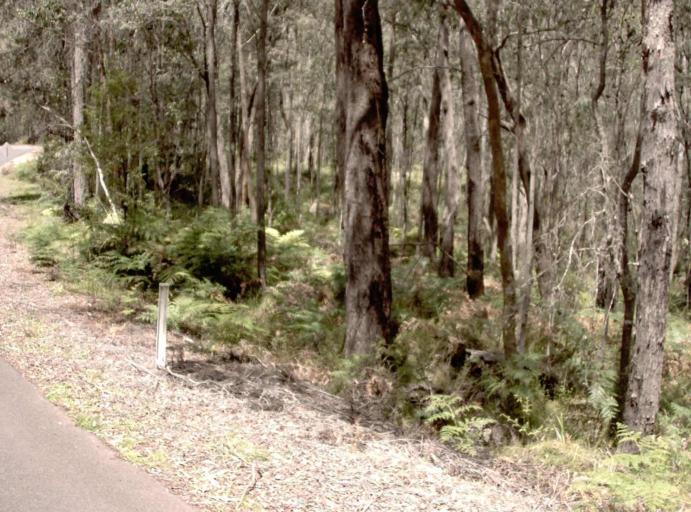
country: AU
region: New South Wales
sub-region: Bombala
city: Bombala
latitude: -37.4389
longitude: 148.9808
